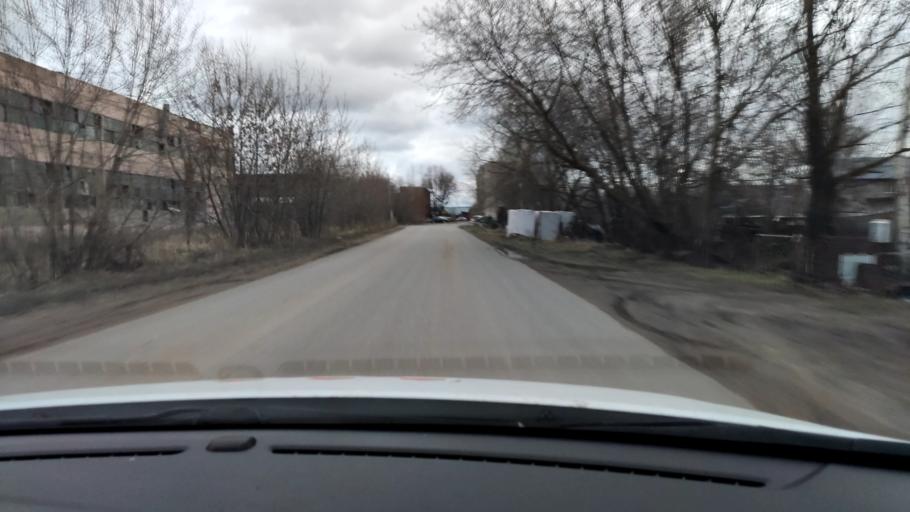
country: RU
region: Tatarstan
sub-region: Gorod Kazan'
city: Kazan
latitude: 55.7210
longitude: 49.0927
